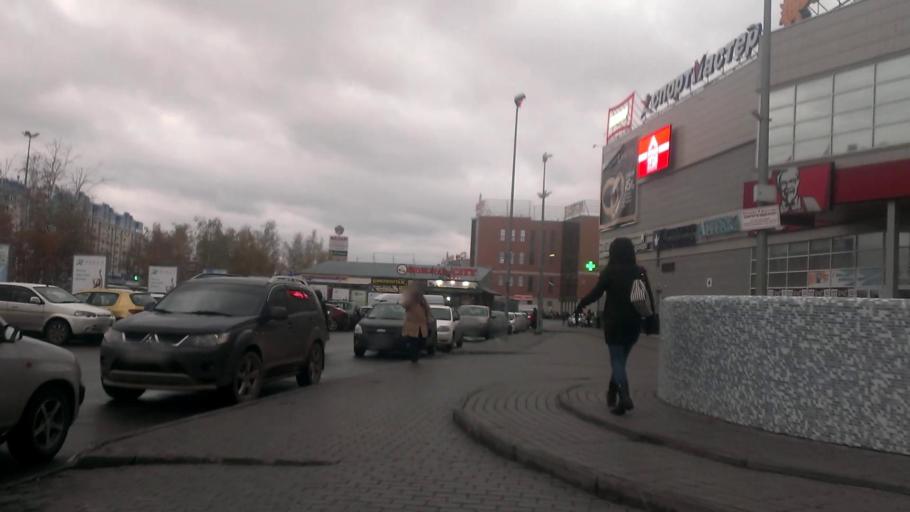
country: RU
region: Altai Krai
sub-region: Gorod Barnaulskiy
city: Barnaul
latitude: 53.3592
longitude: 83.6988
